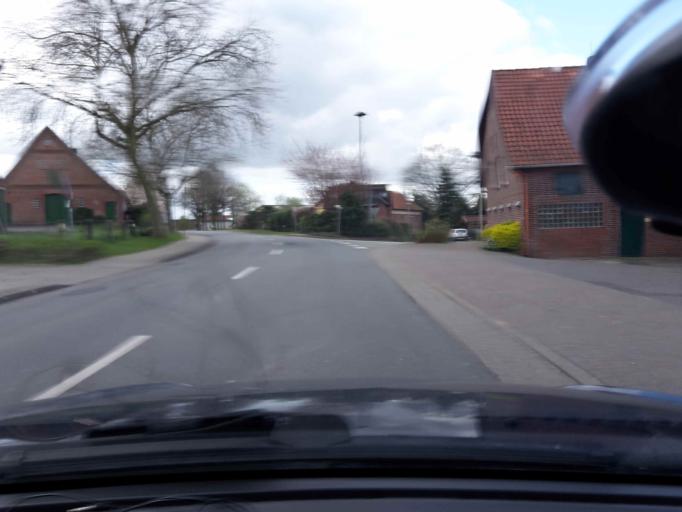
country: DE
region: Lower Saxony
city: Nottensdorf
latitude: 53.4812
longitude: 9.6210
